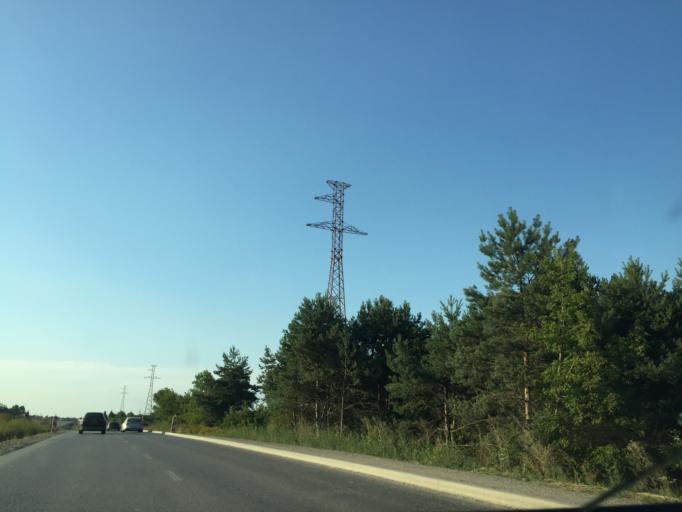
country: PL
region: Masovian Voivodeship
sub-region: Powiat grojecki
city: Grojec
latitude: 51.9219
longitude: 20.8527
